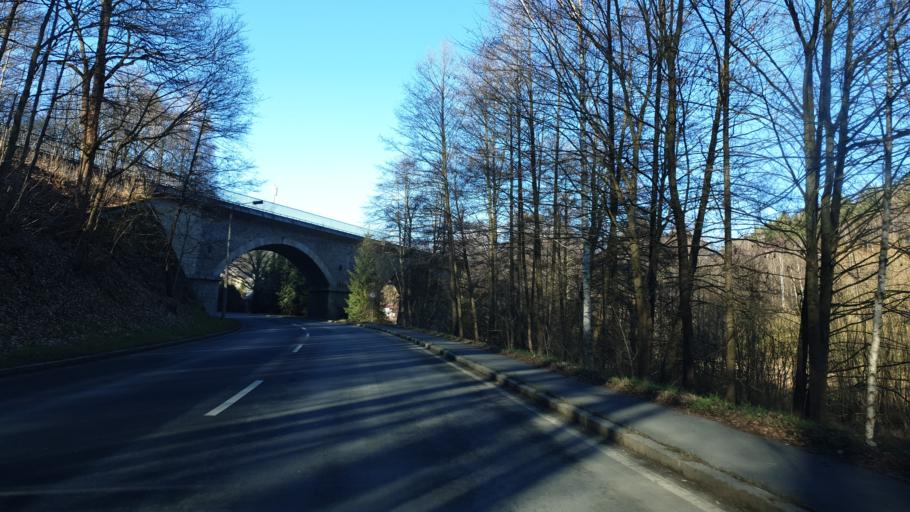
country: DE
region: Saxony
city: Adorf
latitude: 50.2983
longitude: 12.2557
